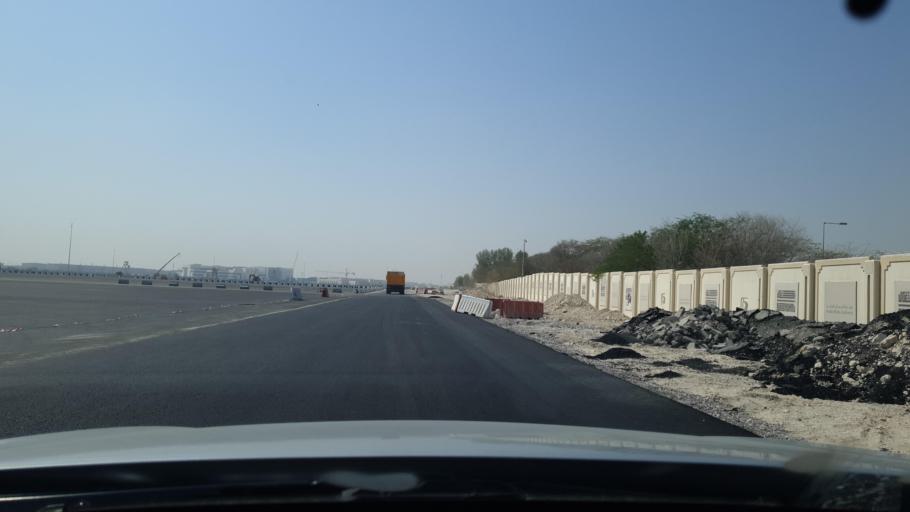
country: QA
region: Baladiyat ad Dawhah
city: Doha
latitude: 25.2280
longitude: 51.5277
